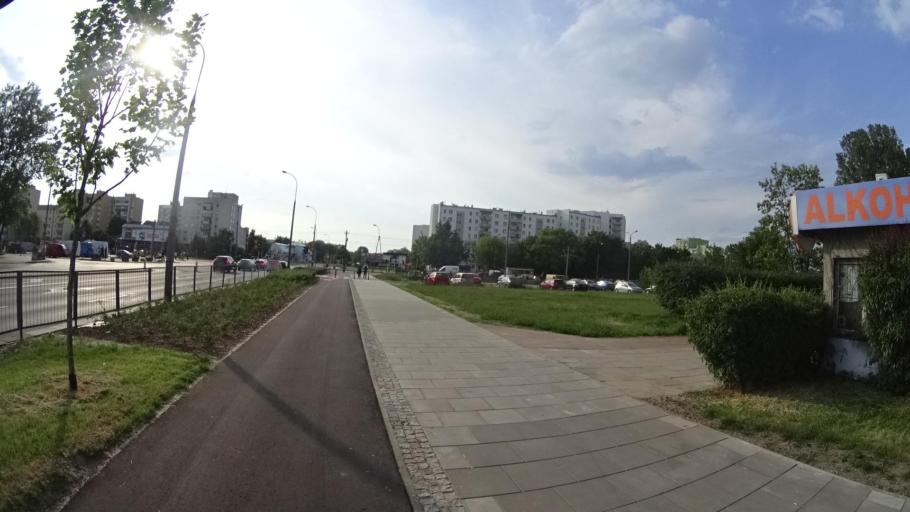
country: PL
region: Masovian Voivodeship
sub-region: Warszawa
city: Bemowo
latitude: 52.2568
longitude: 20.9212
